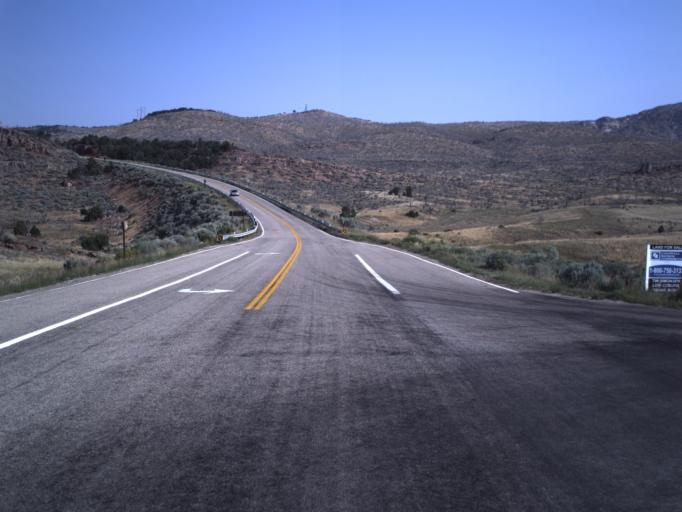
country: US
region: Utah
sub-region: Daggett County
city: Manila
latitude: 40.9350
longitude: -109.4056
